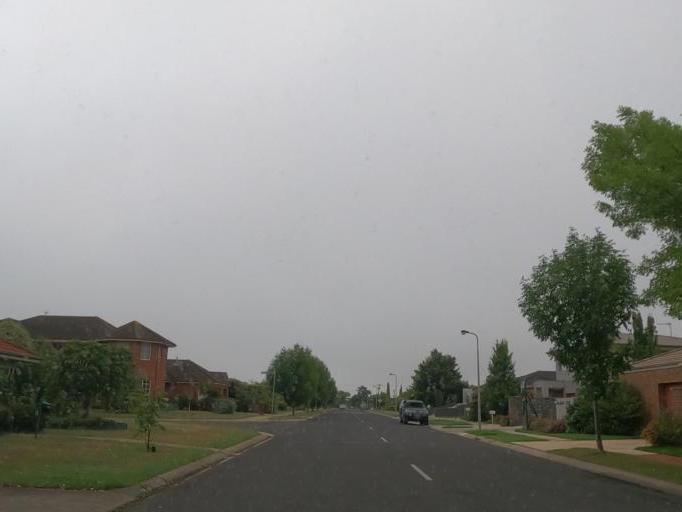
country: AU
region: Victoria
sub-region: Ballarat North
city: Newington
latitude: -37.5485
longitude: 143.7945
